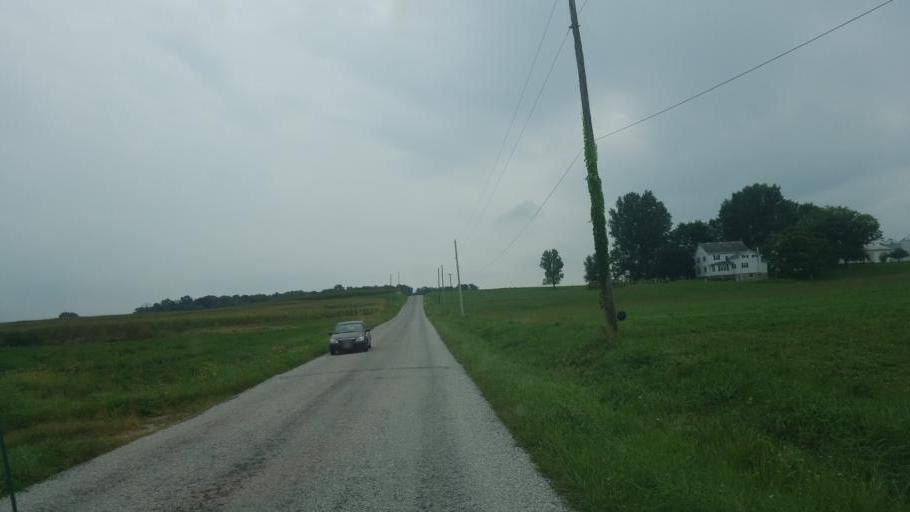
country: US
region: Ohio
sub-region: Wayne County
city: Creston
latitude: 40.9385
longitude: -81.8504
